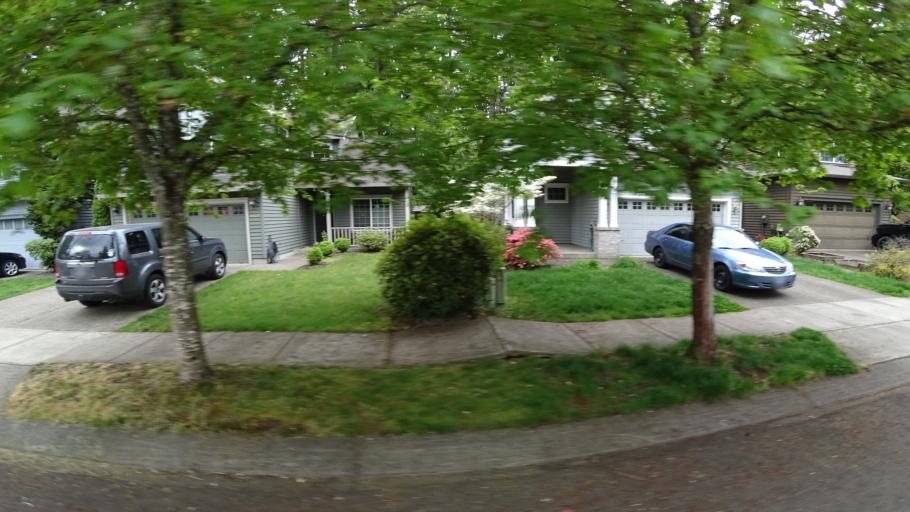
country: US
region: Oregon
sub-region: Washington County
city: Hillsboro
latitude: 45.5355
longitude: -122.9865
